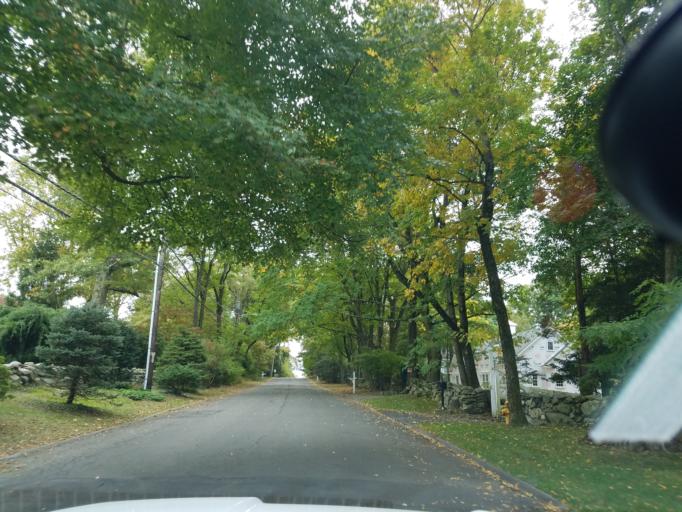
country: US
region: Connecticut
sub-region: Fairfield County
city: Stamford
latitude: 41.0747
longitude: -73.5470
